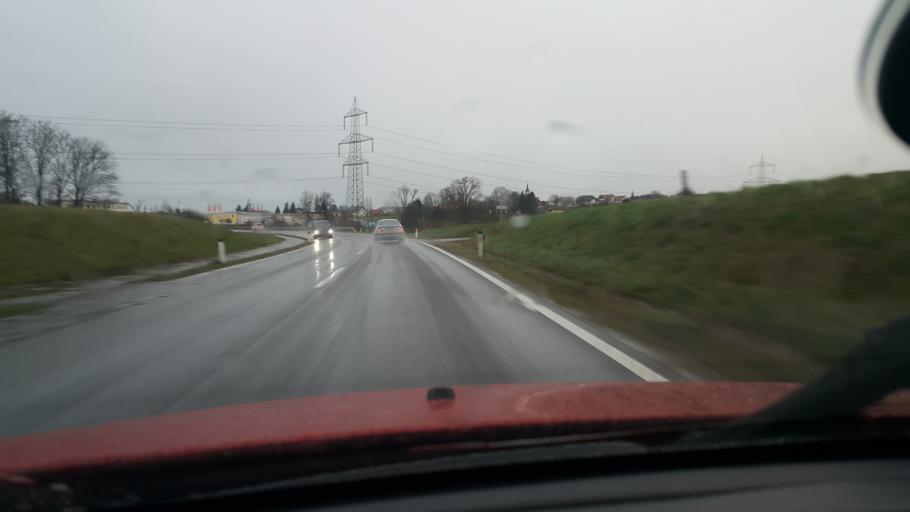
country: AT
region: Styria
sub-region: Politischer Bezirk Deutschlandsberg
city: Preding
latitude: 46.8529
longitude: 15.4169
